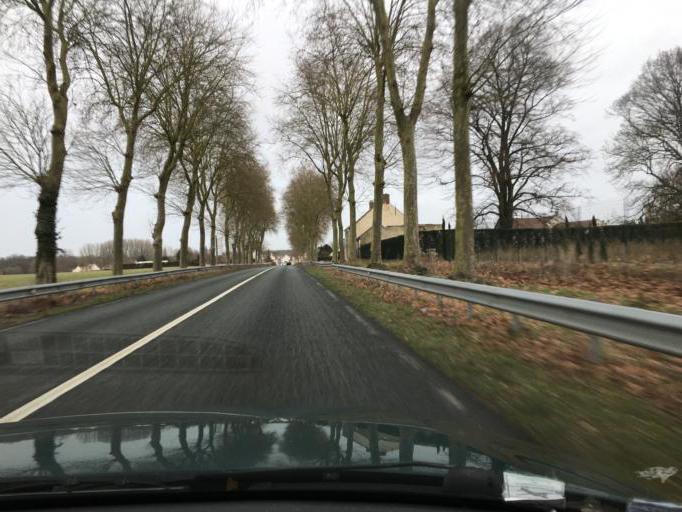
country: FR
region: Picardie
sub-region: Departement de l'Oise
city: La Chapelle-en-Serval
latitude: 49.1481
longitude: 2.5444
